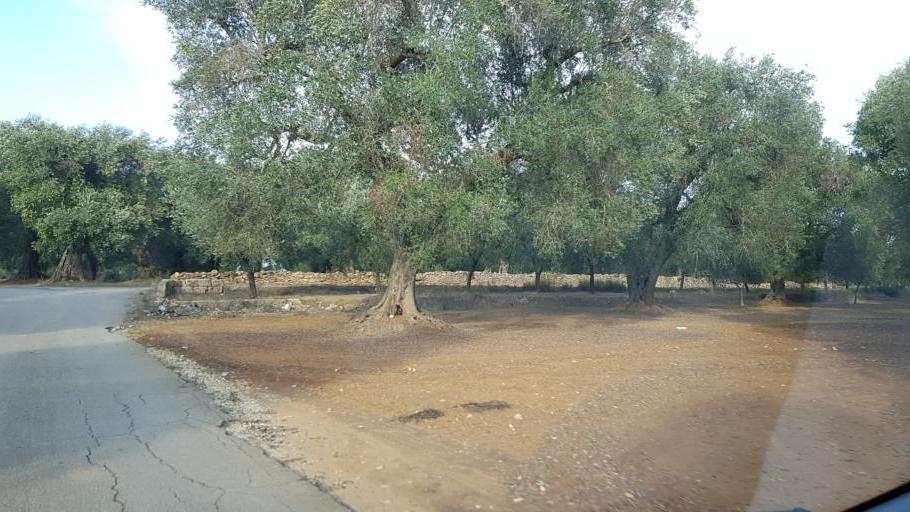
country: IT
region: Apulia
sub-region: Provincia di Brindisi
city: Oria
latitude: 40.5095
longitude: 17.6712
